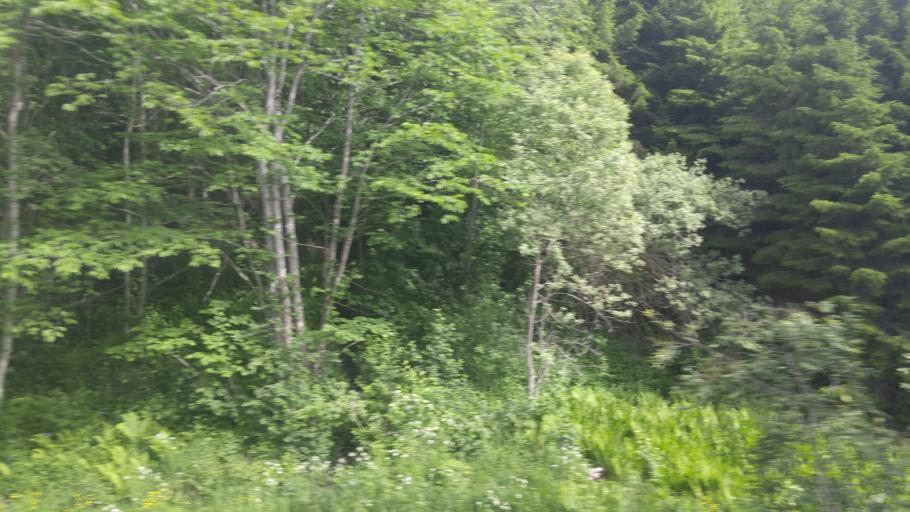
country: NO
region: Sor-Trondelag
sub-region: Midtre Gauldal
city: Storen
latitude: 63.0203
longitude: 10.4262
